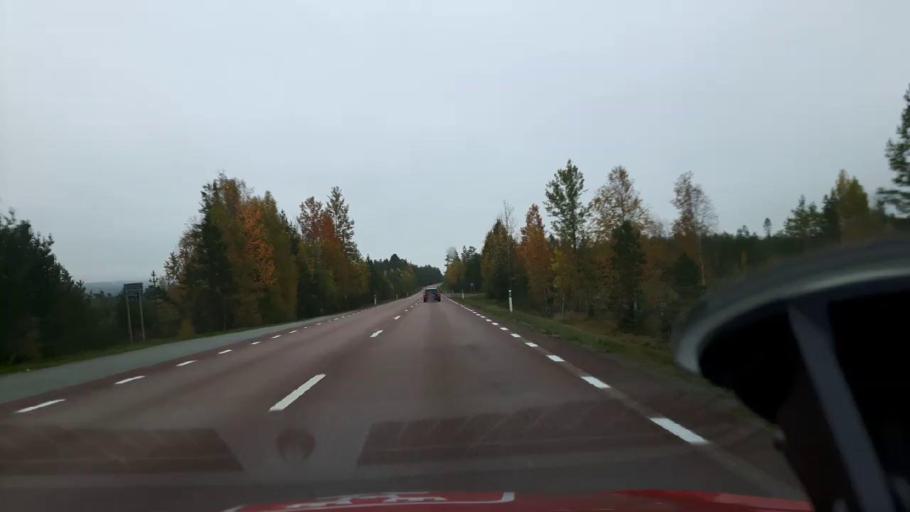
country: SE
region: Jaemtland
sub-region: Bergs Kommun
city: Hoverberg
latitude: 62.4527
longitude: 14.5555
